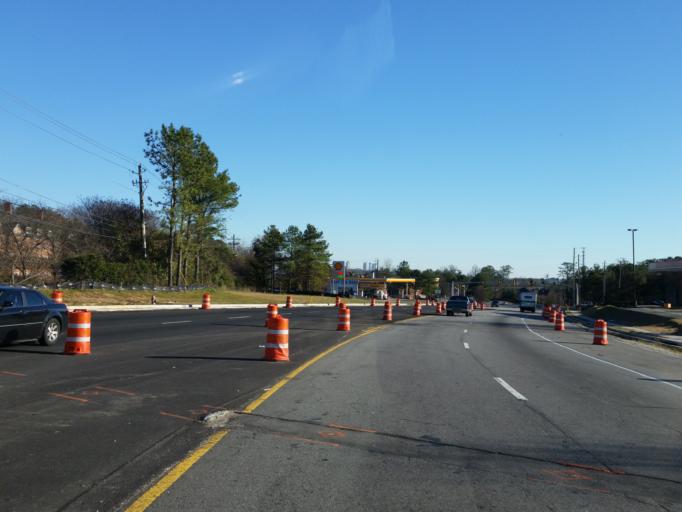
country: US
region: Georgia
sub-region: Cobb County
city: Vinings
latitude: 33.8420
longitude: -84.4861
